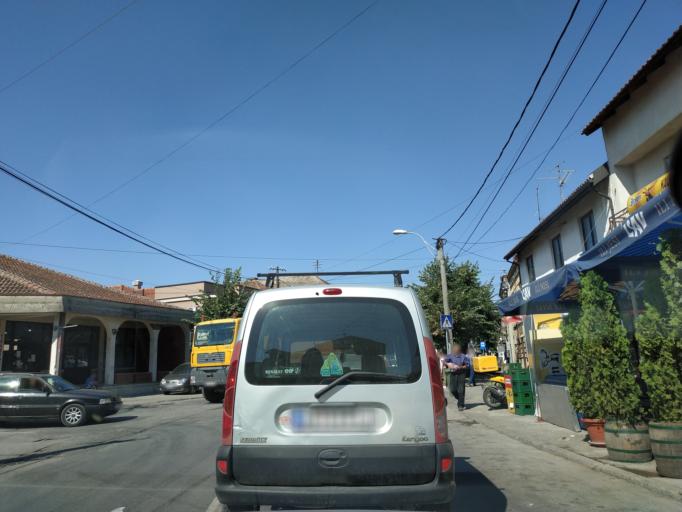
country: RS
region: Central Serbia
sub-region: Sumadijski Okrug
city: Arangelovac
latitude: 44.2992
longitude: 20.5747
